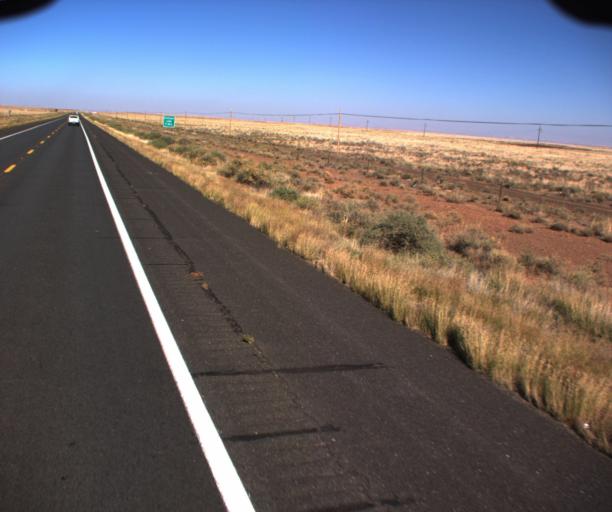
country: US
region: Arizona
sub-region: Coconino County
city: Flagstaff
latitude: 35.6711
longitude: -111.5101
